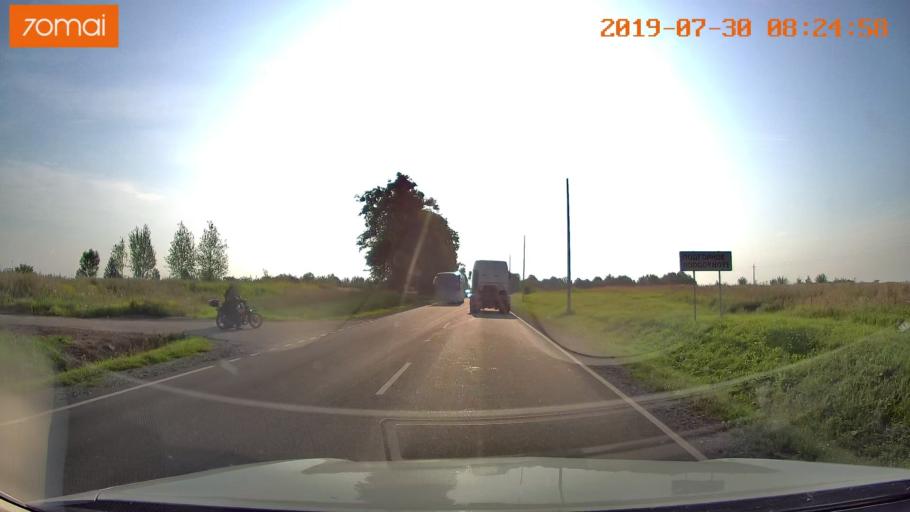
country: RU
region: Kaliningrad
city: Chernyakhovsk
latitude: 54.6238
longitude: 21.5700
